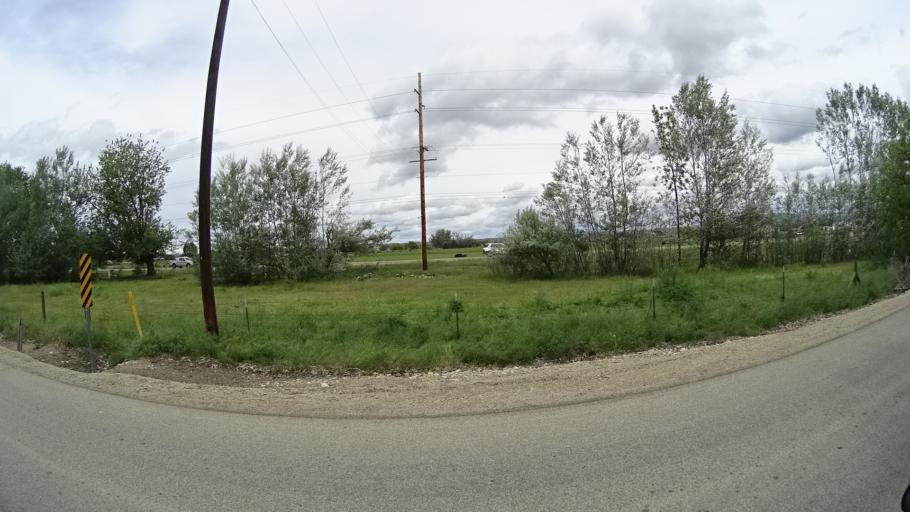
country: US
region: Idaho
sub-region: Ada County
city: Star
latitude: 43.6913
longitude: -116.4281
